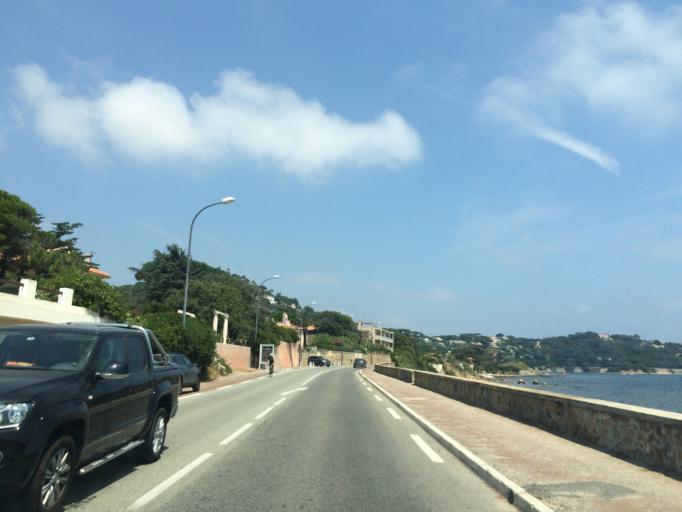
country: FR
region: Provence-Alpes-Cote d'Azur
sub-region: Departement du Var
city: Sainte-Maxime
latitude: 43.3091
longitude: 6.6500
